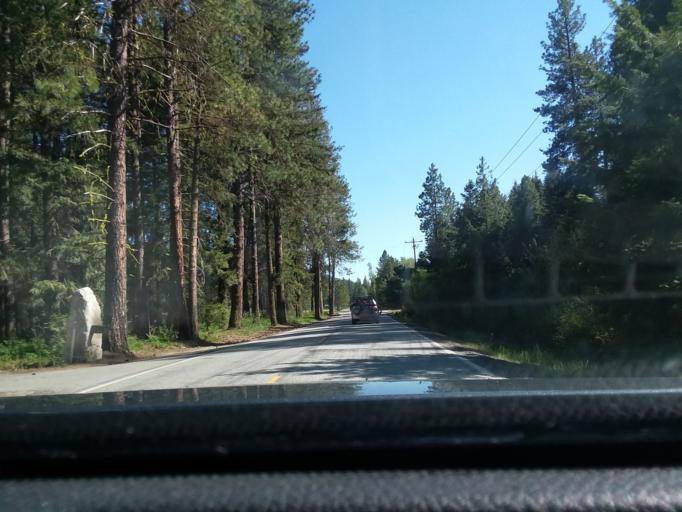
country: US
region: Washington
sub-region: Chelan County
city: Leavenworth
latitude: 47.7711
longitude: -120.6666
